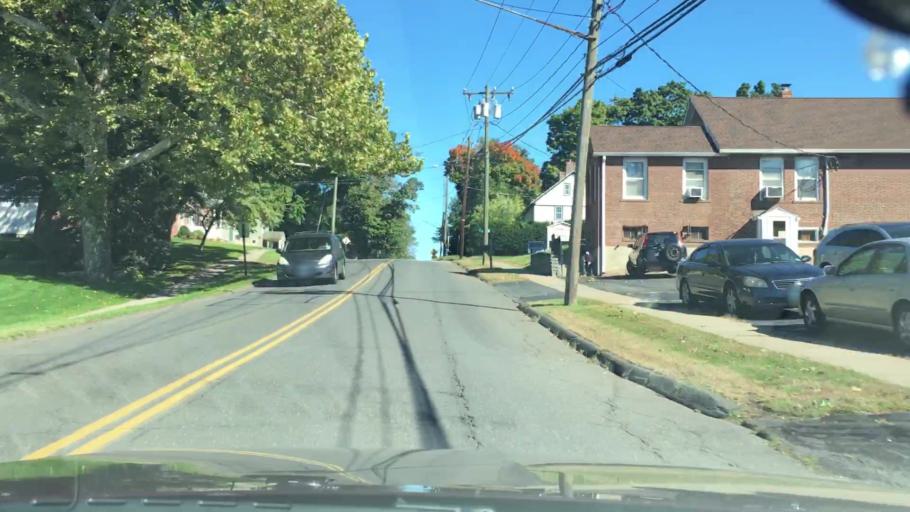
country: US
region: Connecticut
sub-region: Hartford County
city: Kensington
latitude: 41.6178
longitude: -72.7205
